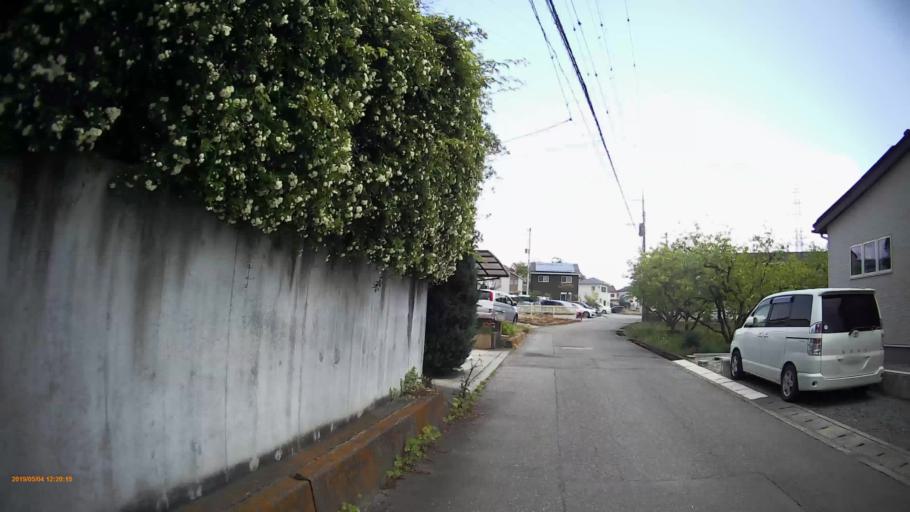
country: JP
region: Yamanashi
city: Ryuo
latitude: 35.6790
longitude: 138.5027
